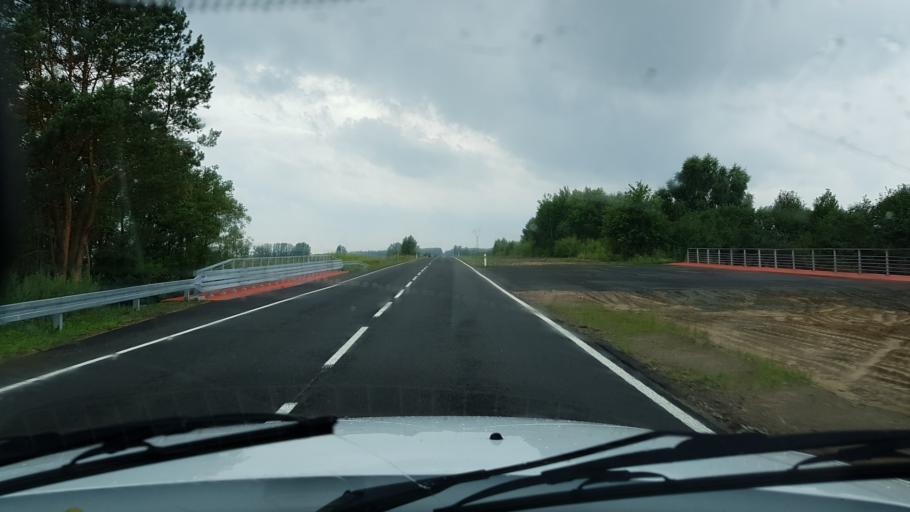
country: PL
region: West Pomeranian Voivodeship
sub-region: Powiat goleniowski
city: Maszewo
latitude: 53.4302
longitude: 14.9721
